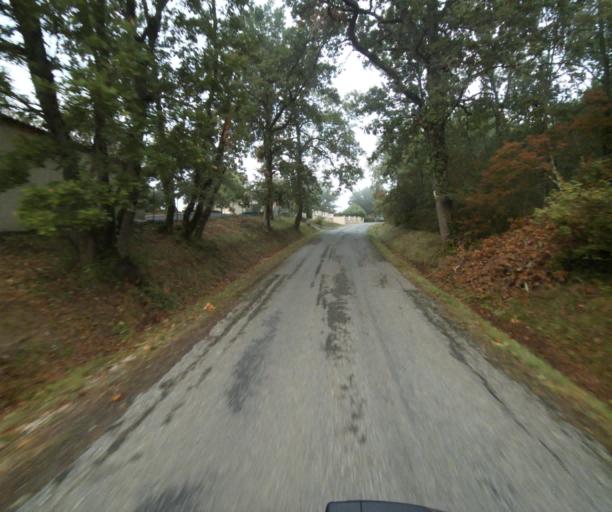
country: FR
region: Midi-Pyrenees
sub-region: Departement du Tarn-et-Garonne
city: Orgueil
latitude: 43.9306
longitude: 1.4229
